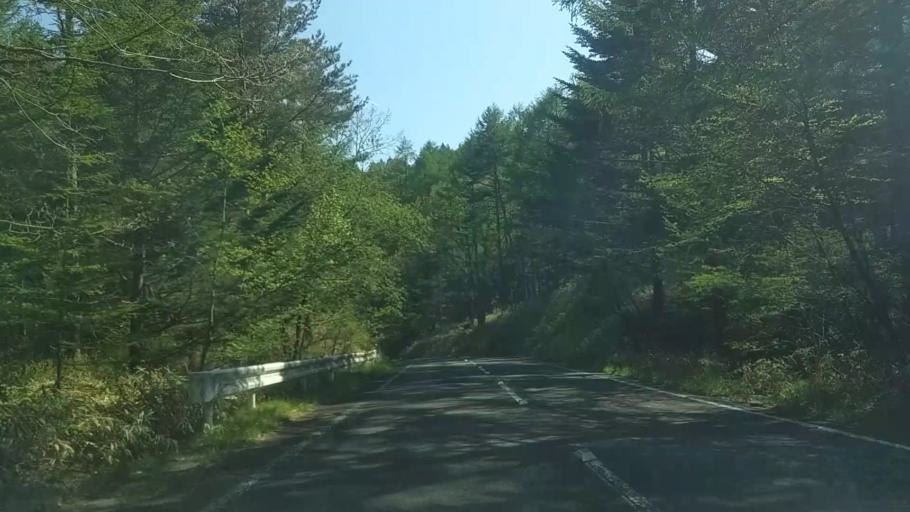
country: JP
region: Yamanashi
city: Nirasaki
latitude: 35.9237
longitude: 138.4015
